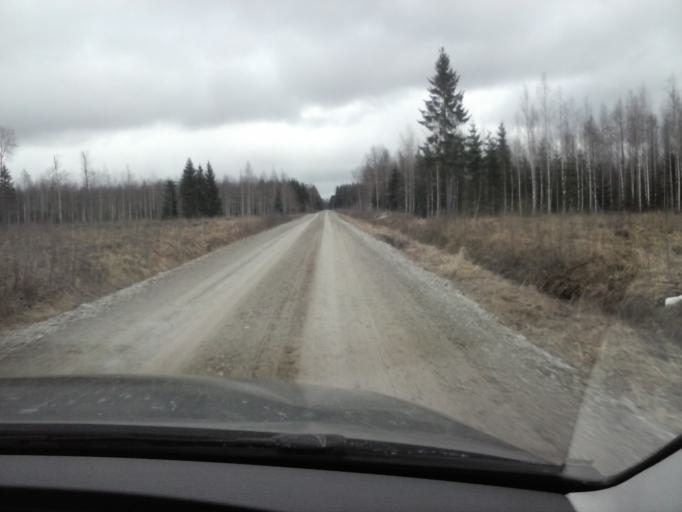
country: EE
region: Jogevamaa
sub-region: Mustvee linn
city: Mustvee
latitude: 59.0596
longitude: 26.8393
